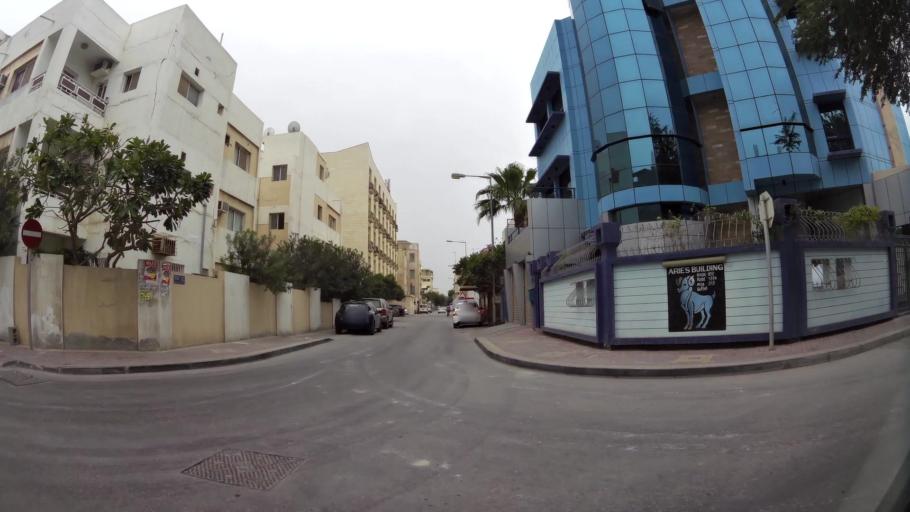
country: BH
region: Manama
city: Manama
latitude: 26.2216
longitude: 50.5663
